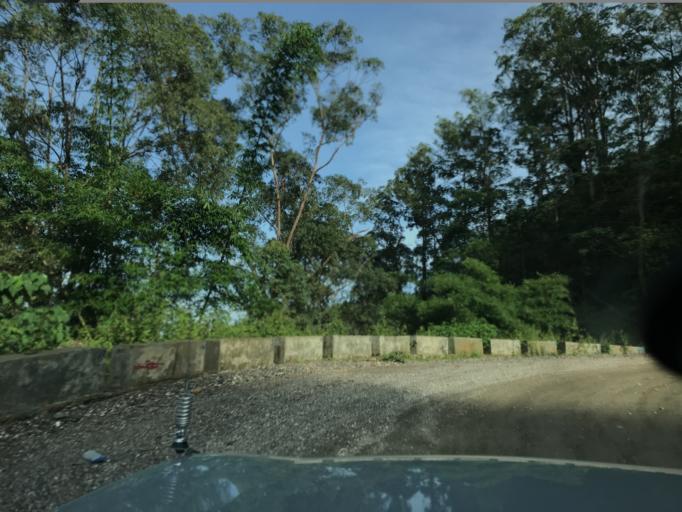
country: TL
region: Aileu
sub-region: Aileu Villa
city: Aileu
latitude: -8.6665
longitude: 125.5526
